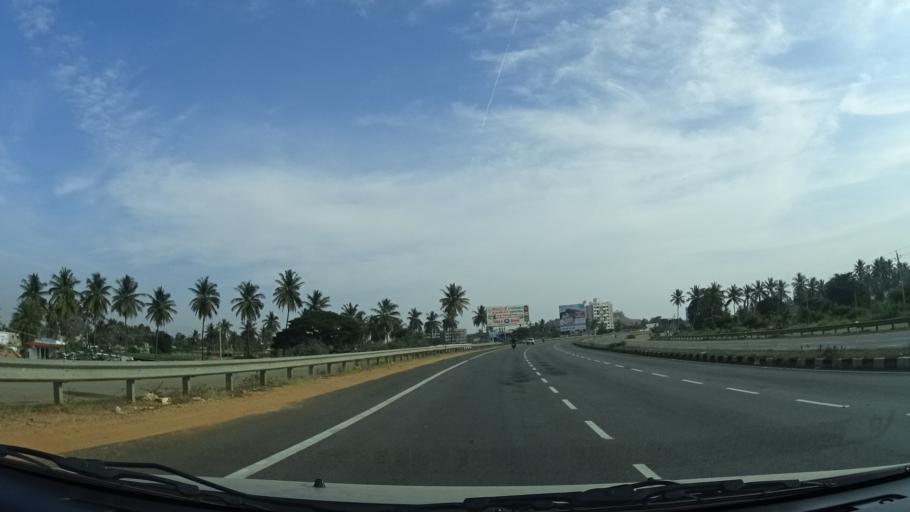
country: IN
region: Karnataka
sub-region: Bangalore Rural
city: Devanhalli
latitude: 13.2526
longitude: 77.7075
